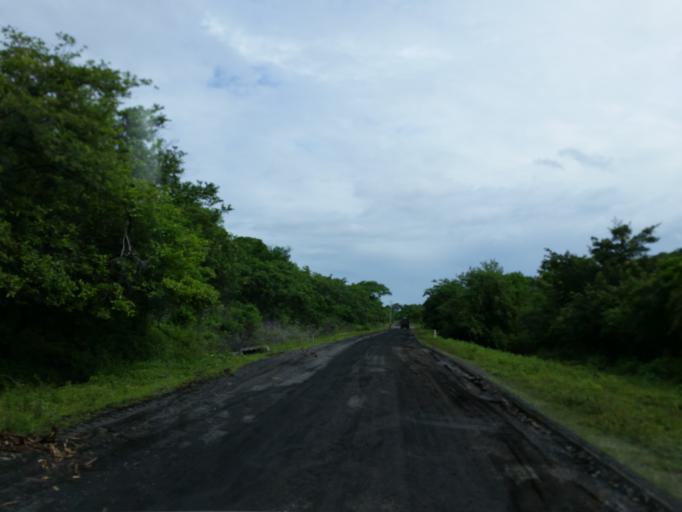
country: NI
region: Leon
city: La Paz Centro
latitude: 12.3728
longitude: -86.6631
